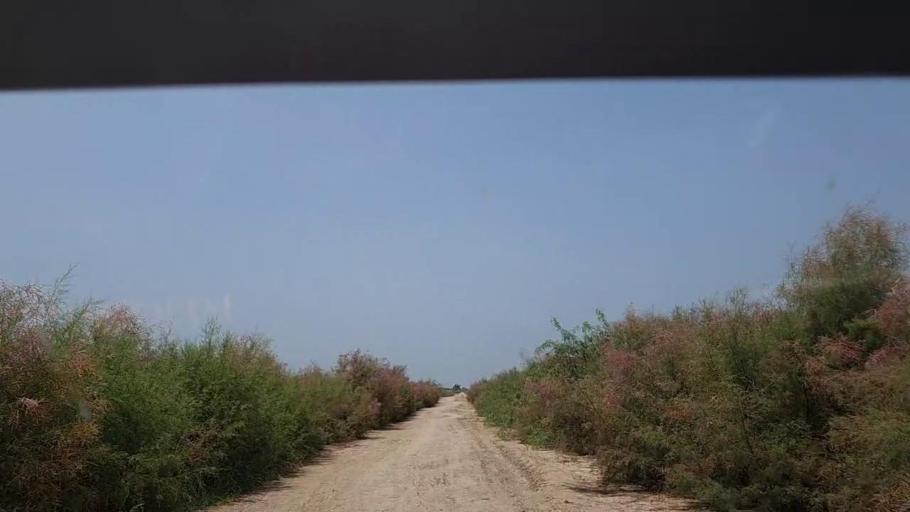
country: PK
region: Sindh
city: Adilpur
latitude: 27.8965
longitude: 69.2400
